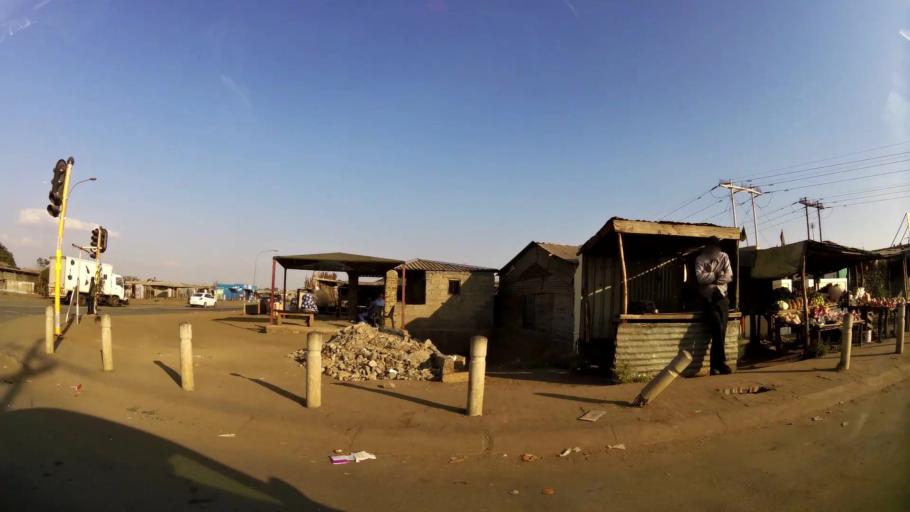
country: ZA
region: Gauteng
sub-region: Ekurhuleni Metropolitan Municipality
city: Tembisa
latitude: -25.9813
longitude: 28.2121
